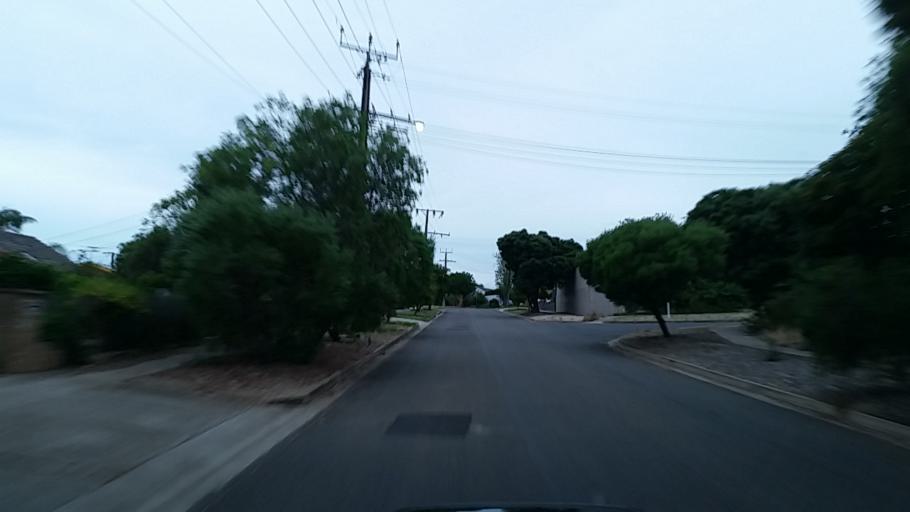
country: AU
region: South Australia
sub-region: Adelaide
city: Port Noarlunga
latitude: -35.1267
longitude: 138.4826
